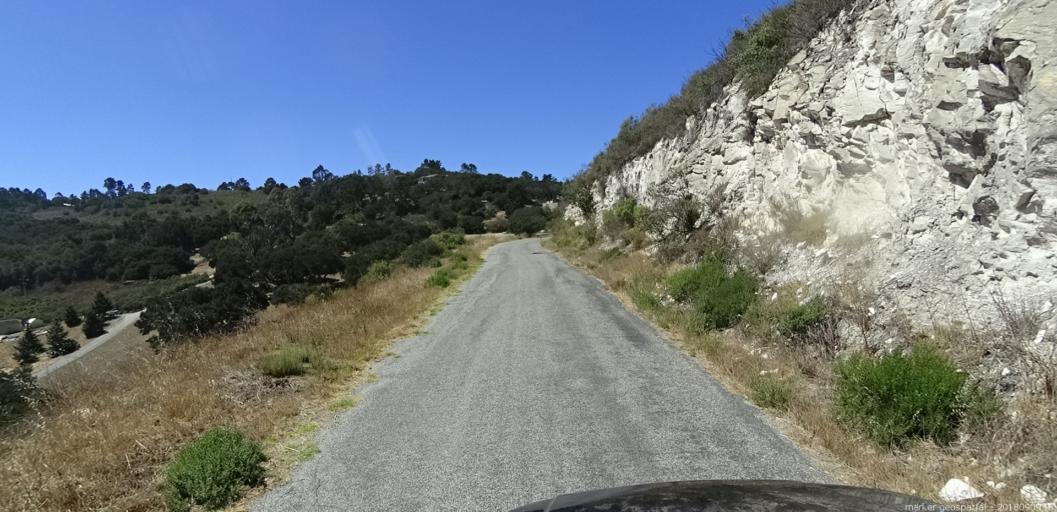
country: US
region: California
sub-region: Monterey County
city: Carmel Valley Village
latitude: 36.5492
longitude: -121.7467
